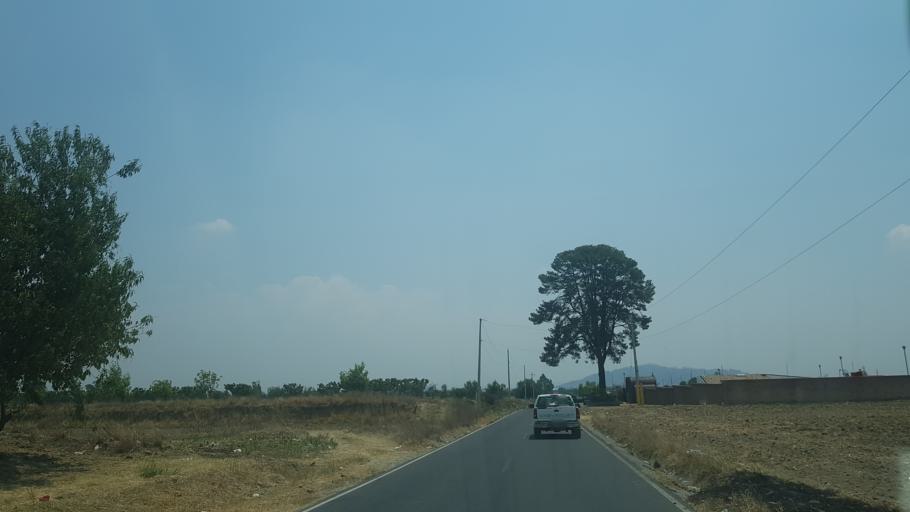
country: MX
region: Puebla
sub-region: San Jeronimo Tecuanipan
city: San Miguel Papaxtla
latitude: 19.0954
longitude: -98.4074
